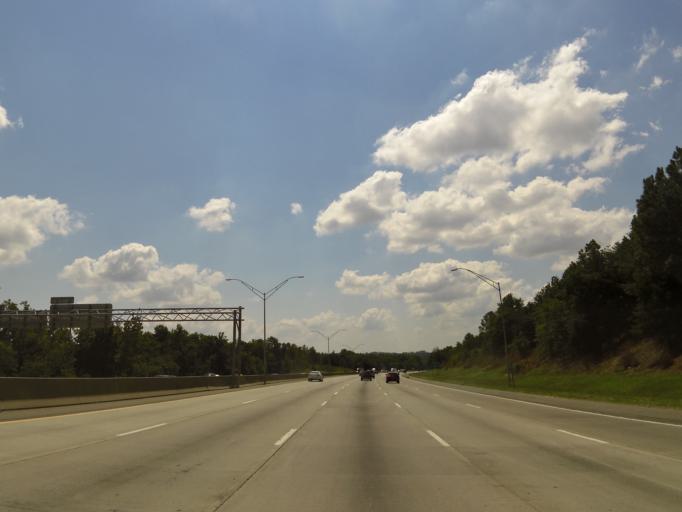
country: US
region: North Carolina
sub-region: Cabarrus County
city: Harrisburg
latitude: 35.3289
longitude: -80.7455
